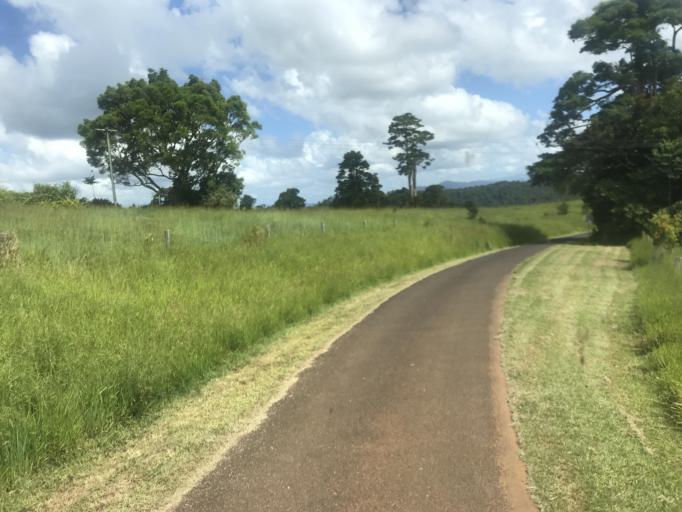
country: AU
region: Queensland
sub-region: Tablelands
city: Ravenshoe
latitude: -17.5468
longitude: 145.6976
